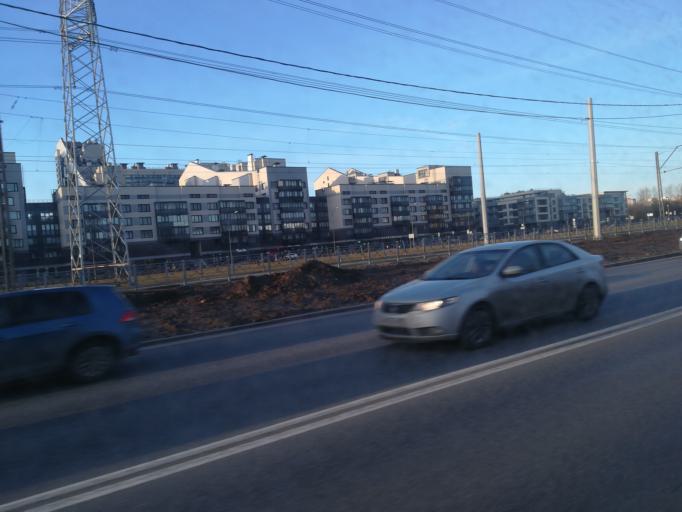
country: RU
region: St.-Petersburg
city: Sosnovaya Polyana
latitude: 59.8466
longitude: 30.1527
